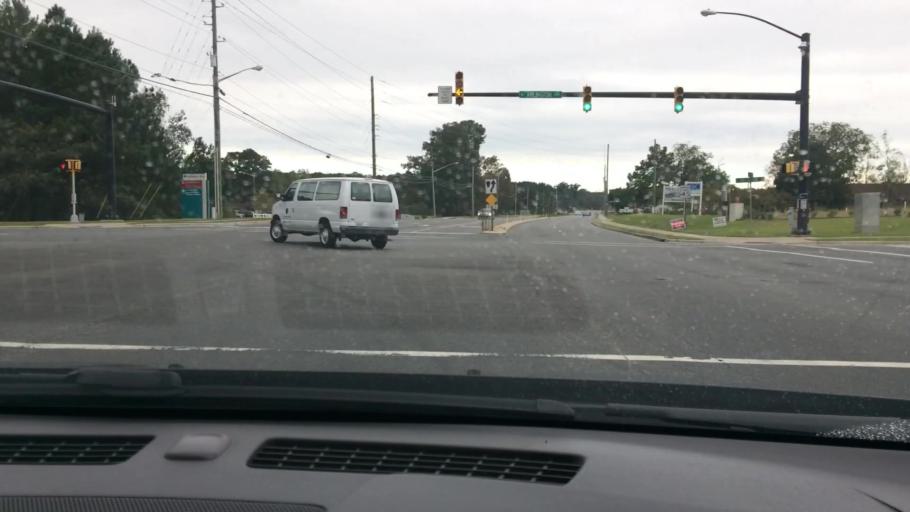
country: US
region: North Carolina
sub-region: Pitt County
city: Greenville
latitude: 35.6158
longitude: -77.4089
